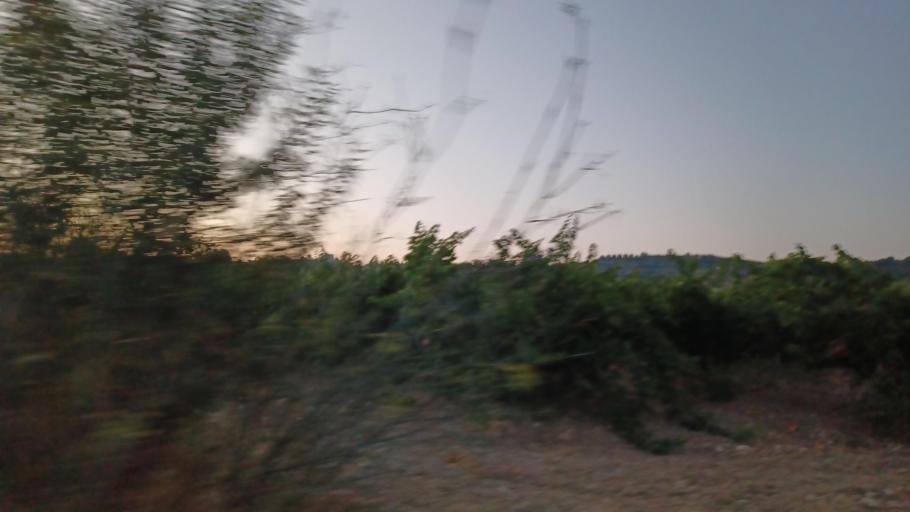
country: CY
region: Pafos
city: Mesogi
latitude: 34.8698
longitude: 32.4974
